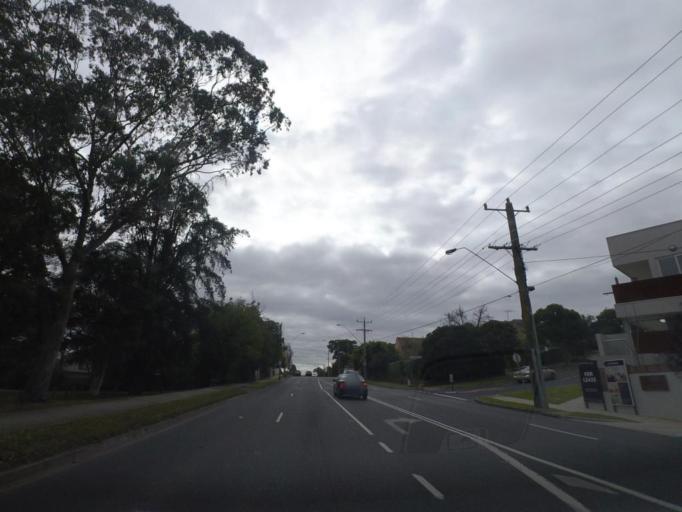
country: AU
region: Victoria
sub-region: Whitehorse
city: Mont Albert North
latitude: -37.8080
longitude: 145.1166
